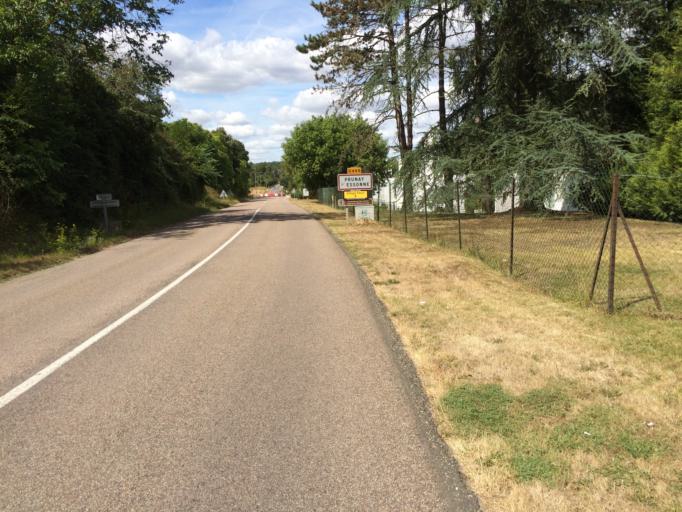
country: FR
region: Ile-de-France
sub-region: Departement de l'Essonne
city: Maisse
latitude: 48.3509
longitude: 2.3814
